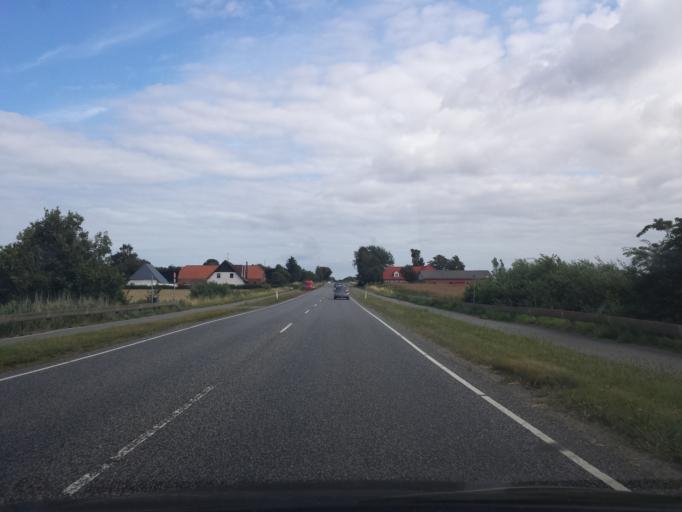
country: DK
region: South Denmark
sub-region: Sonderborg Kommune
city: Guderup
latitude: 54.9761
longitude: 9.8868
